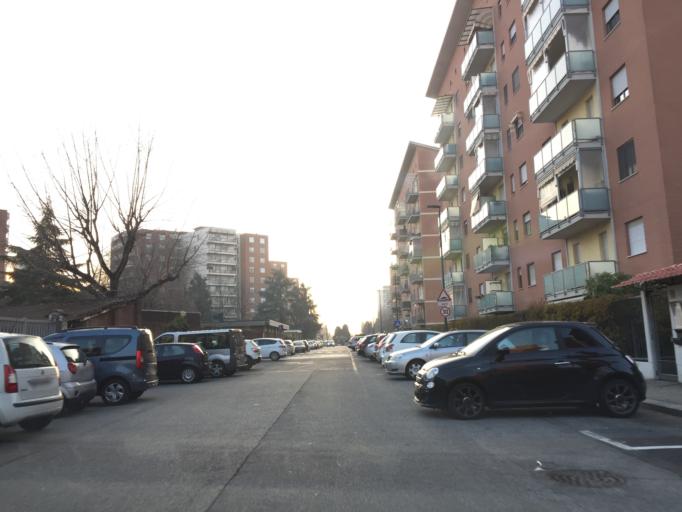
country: IT
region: Piedmont
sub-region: Provincia di Torino
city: Gerbido
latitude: 45.0405
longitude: 7.6218
